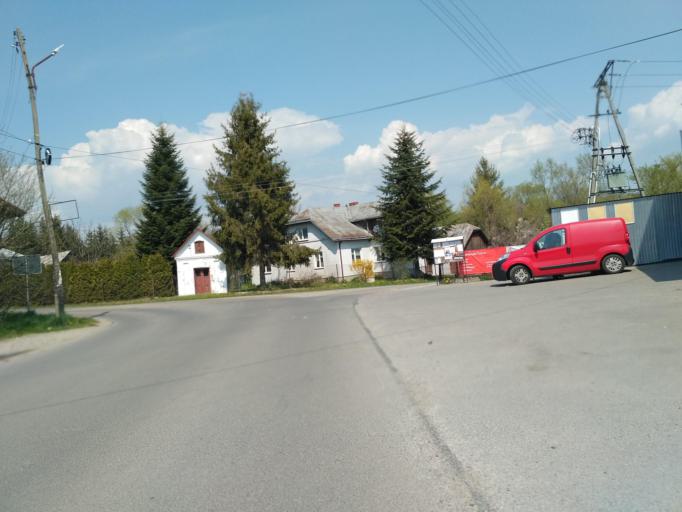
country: PL
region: Subcarpathian Voivodeship
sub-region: Powiat krosnienski
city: Chorkowka
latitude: 49.6594
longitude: 21.6524
